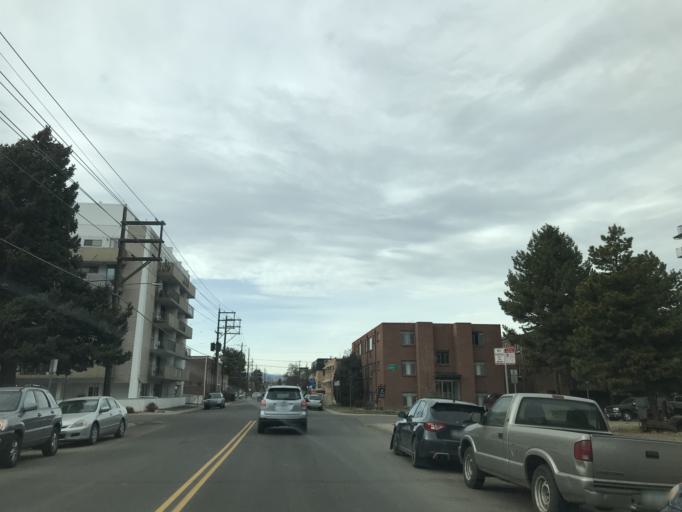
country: US
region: Colorado
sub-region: Arapahoe County
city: Glendale
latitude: 39.7293
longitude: -104.9312
